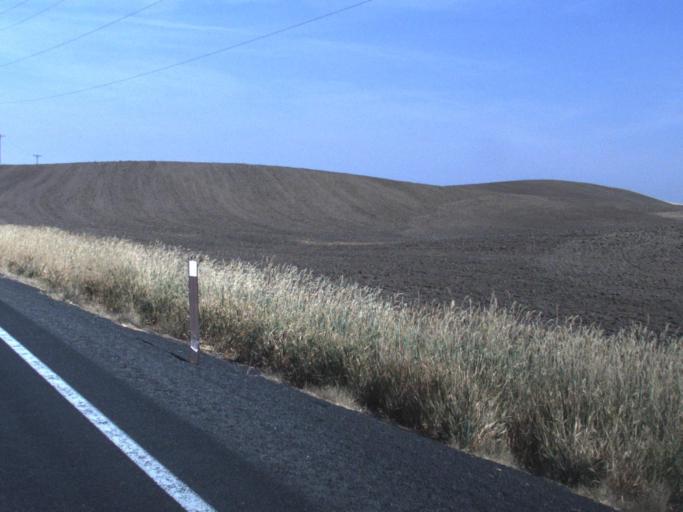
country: US
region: Washington
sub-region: Whitman County
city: Colfax
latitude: 47.0579
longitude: -117.1535
